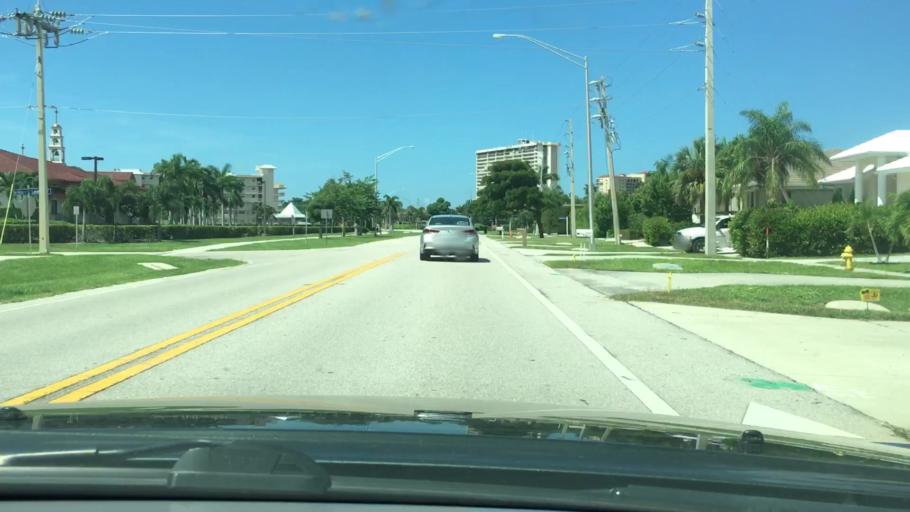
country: US
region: Florida
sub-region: Collier County
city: Marco
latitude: 25.9371
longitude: -81.7267
